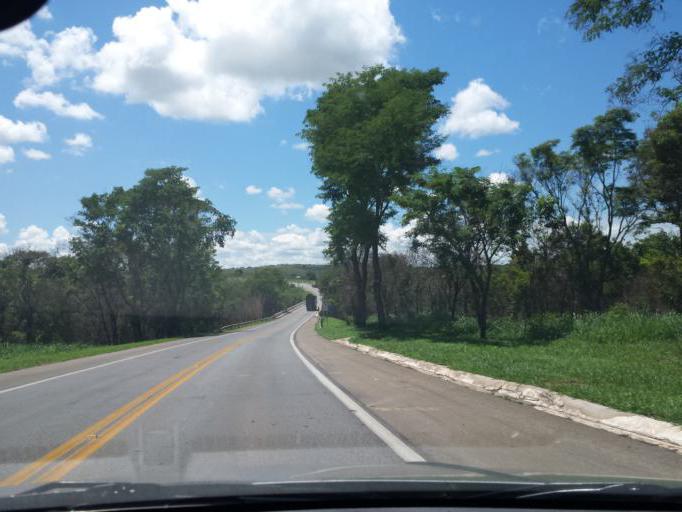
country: BR
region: Goias
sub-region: Cristalina
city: Cristalina
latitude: -16.5352
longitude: -47.7994
